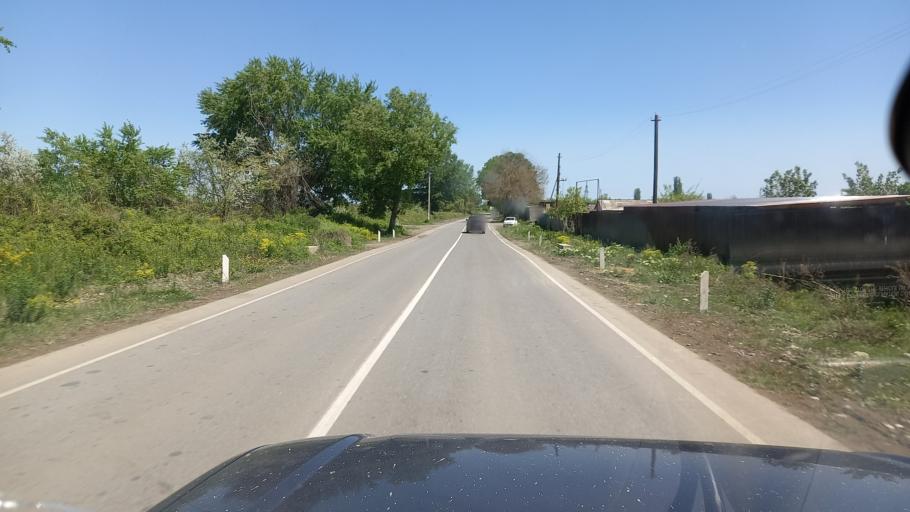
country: RU
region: Dagestan
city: Samur
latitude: 41.8003
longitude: 48.4991
